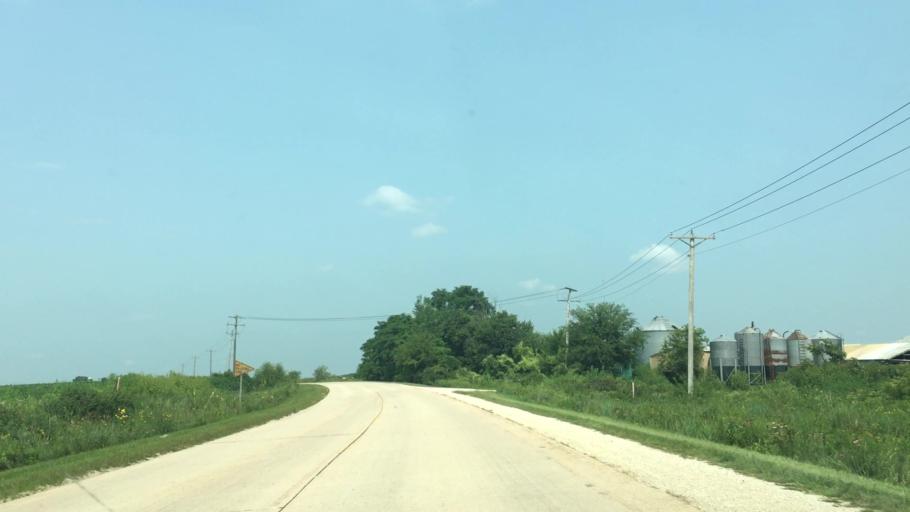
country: US
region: Iowa
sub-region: Fayette County
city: Oelwein
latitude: 42.6654
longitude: -91.8943
